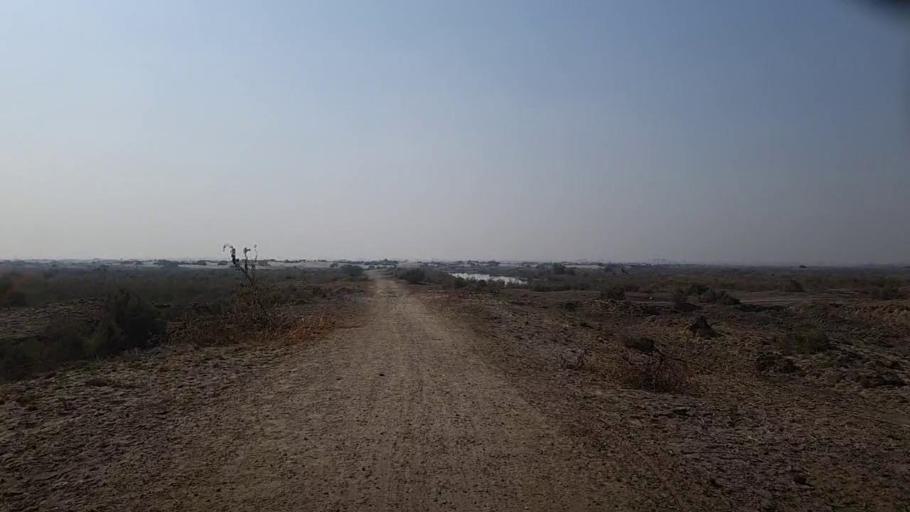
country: PK
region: Sindh
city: Bozdar
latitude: 27.2295
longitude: 68.5917
